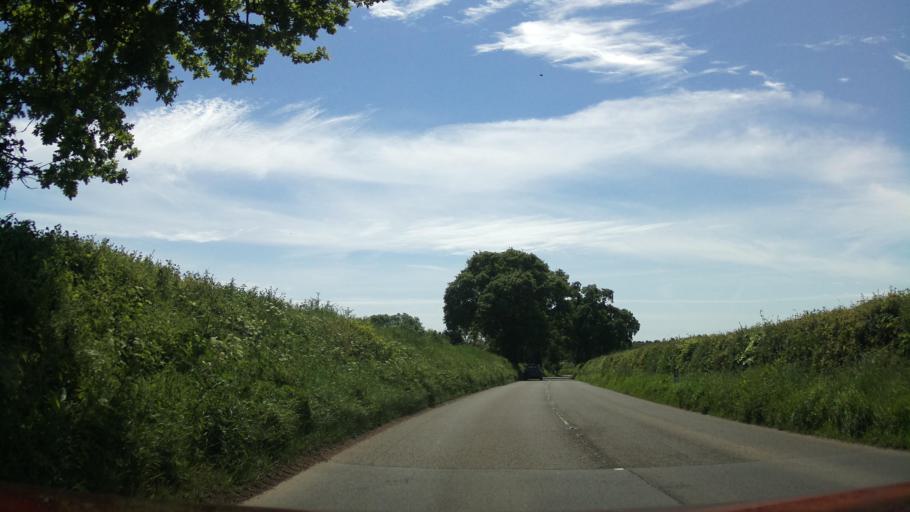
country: GB
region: England
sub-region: Devon
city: Uffculme
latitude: 50.8498
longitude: -3.3243
